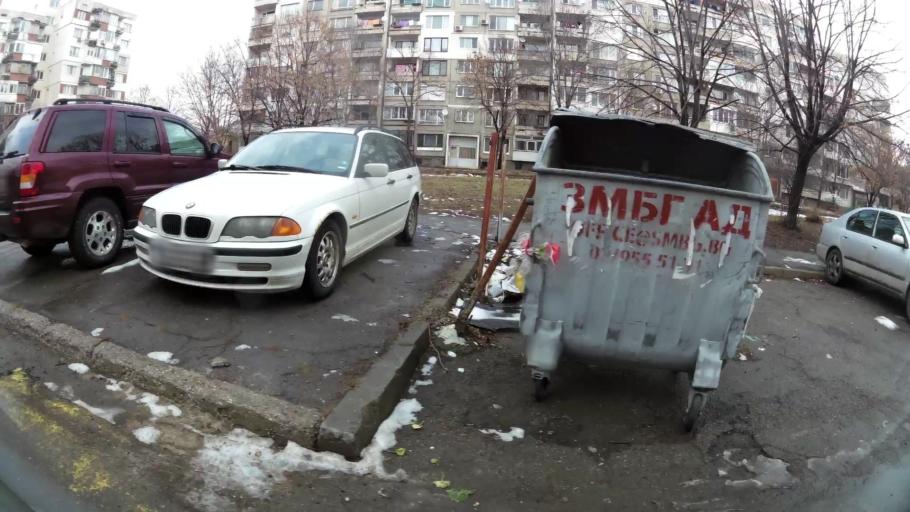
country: BG
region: Sofia-Capital
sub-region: Stolichna Obshtina
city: Sofia
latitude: 42.7114
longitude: 23.2599
